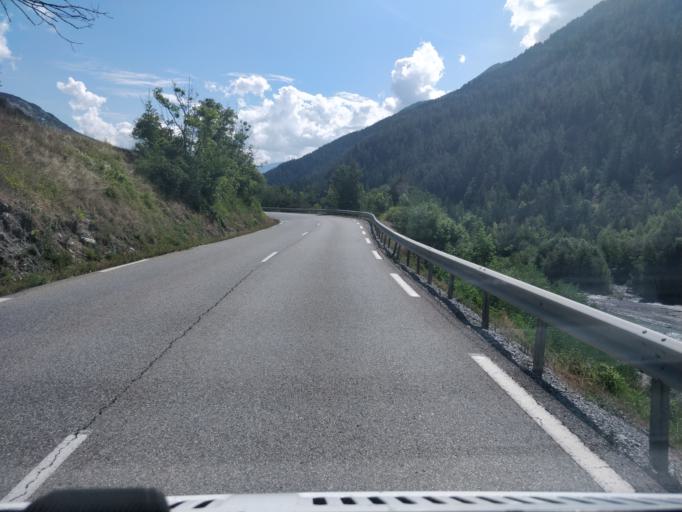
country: FR
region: Provence-Alpes-Cote d'Azur
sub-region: Departement des Alpes-de-Haute-Provence
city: Barcelonnette
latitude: 44.4009
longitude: 6.5159
